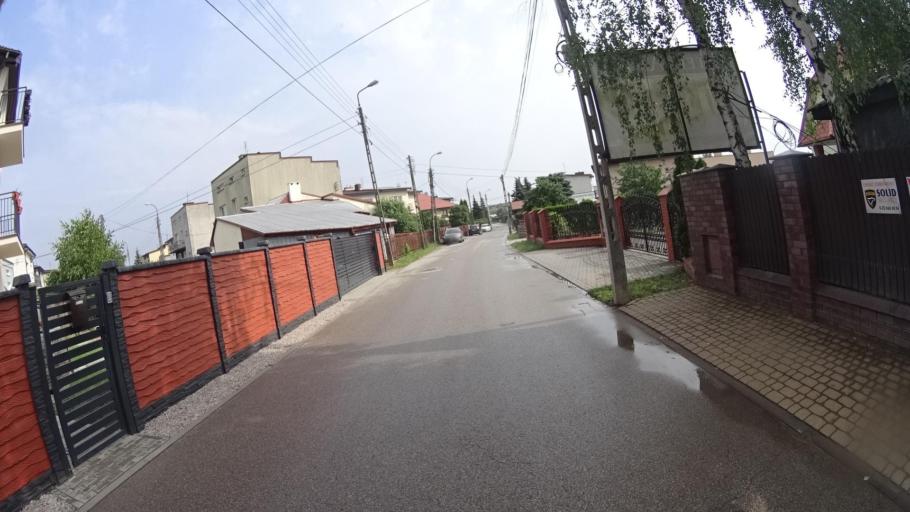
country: PL
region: Masovian Voivodeship
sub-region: Powiat pruszkowski
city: Raszyn
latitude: 52.1637
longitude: 20.9202
